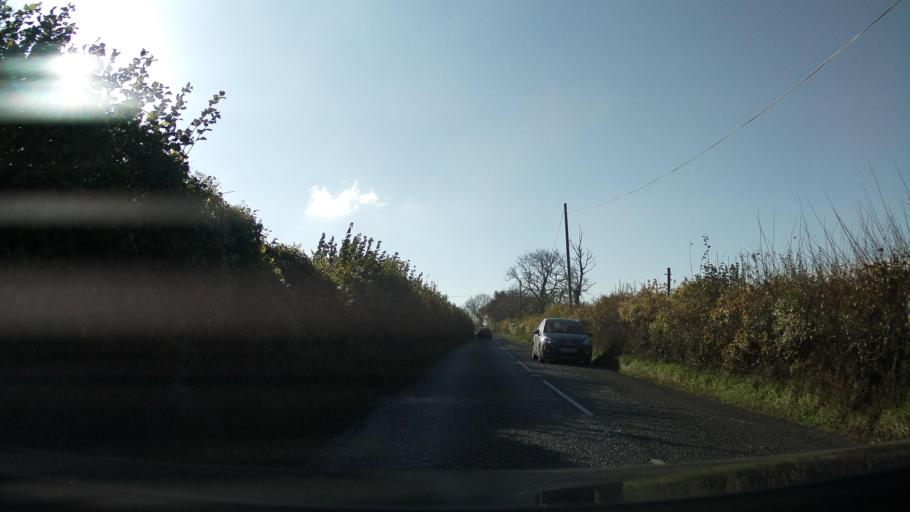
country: GB
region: England
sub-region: Somerset
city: Bruton
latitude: 51.1533
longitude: -2.4190
